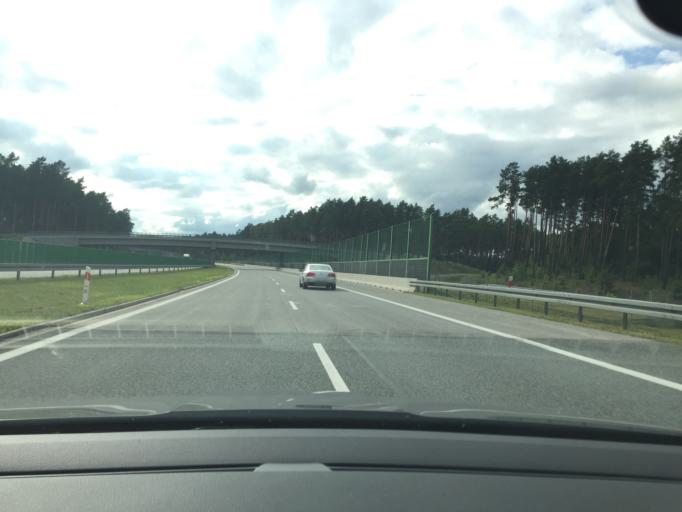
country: PL
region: Lubusz
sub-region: Powiat swiebodzinski
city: Lagow
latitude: 52.3086
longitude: 15.2458
